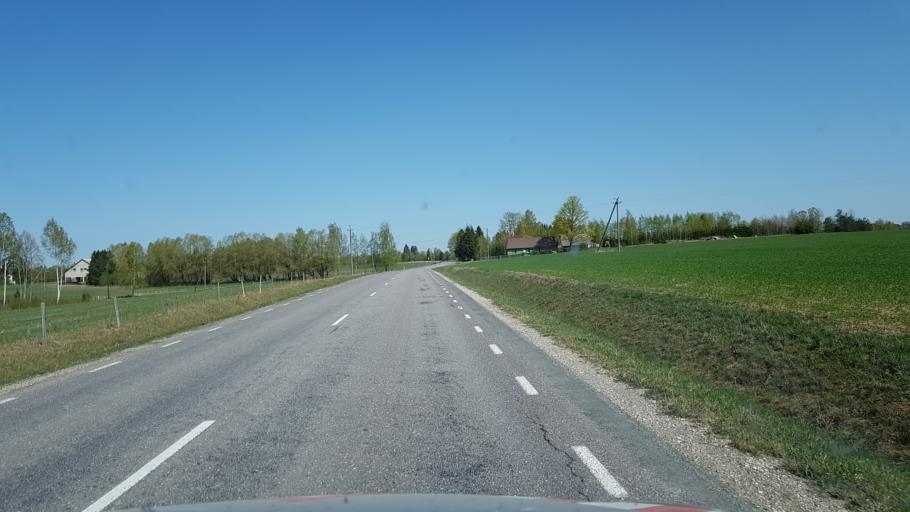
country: EE
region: Viljandimaa
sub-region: Suure-Jaani vald
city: Suure-Jaani
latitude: 58.5092
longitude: 25.4611
